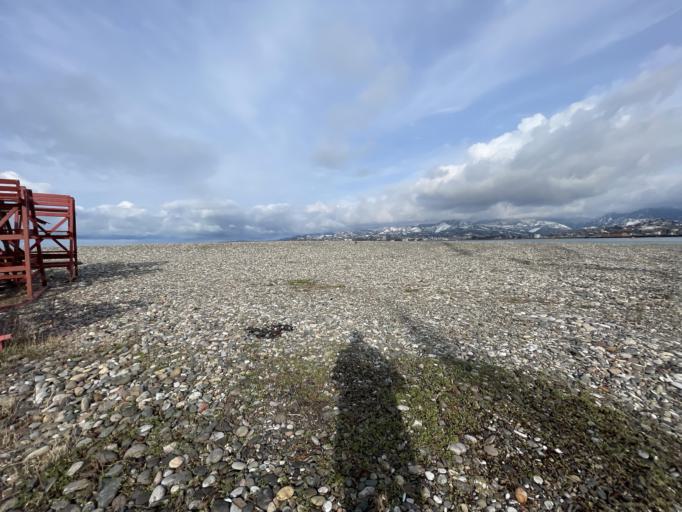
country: GE
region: Ajaria
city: Batumi
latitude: 41.6551
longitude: 41.6439
